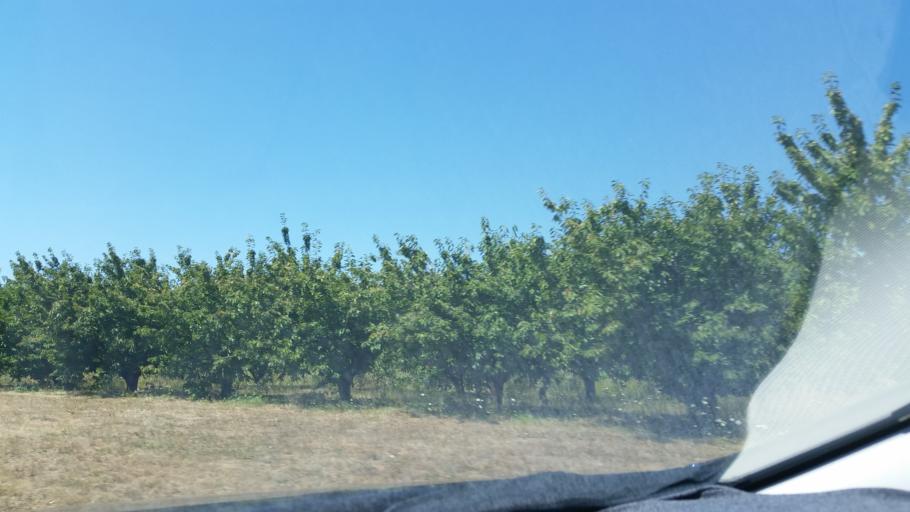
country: US
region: Oregon
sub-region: Clackamas County
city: Wilsonville
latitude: 45.2596
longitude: -122.7802
